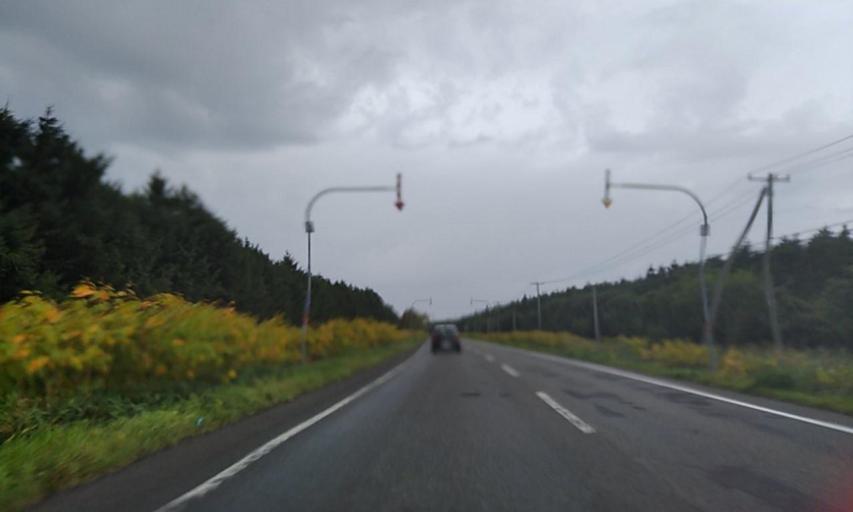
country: JP
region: Hokkaido
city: Nayoro
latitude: 44.8976
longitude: 142.6065
